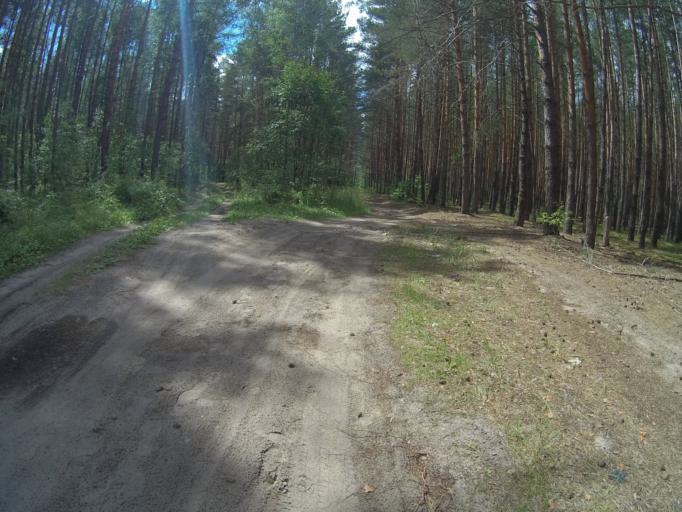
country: RU
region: Vladimir
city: Raduzhnyy
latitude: 56.0605
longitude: 40.3421
